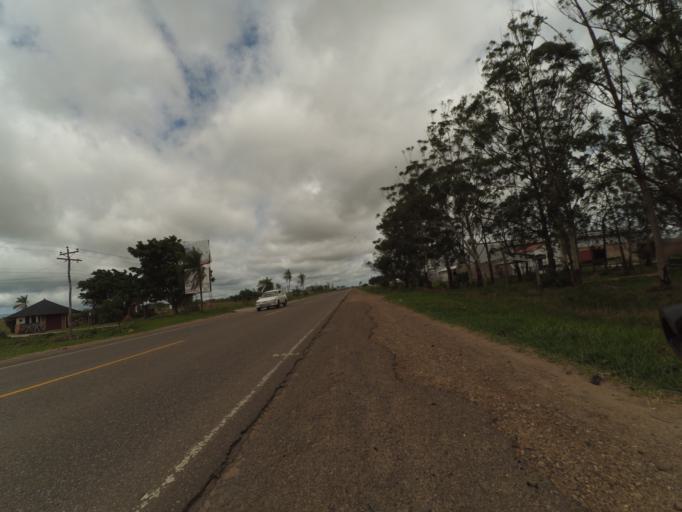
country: BO
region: Santa Cruz
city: Santa Rita
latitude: -17.9026
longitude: -63.2549
